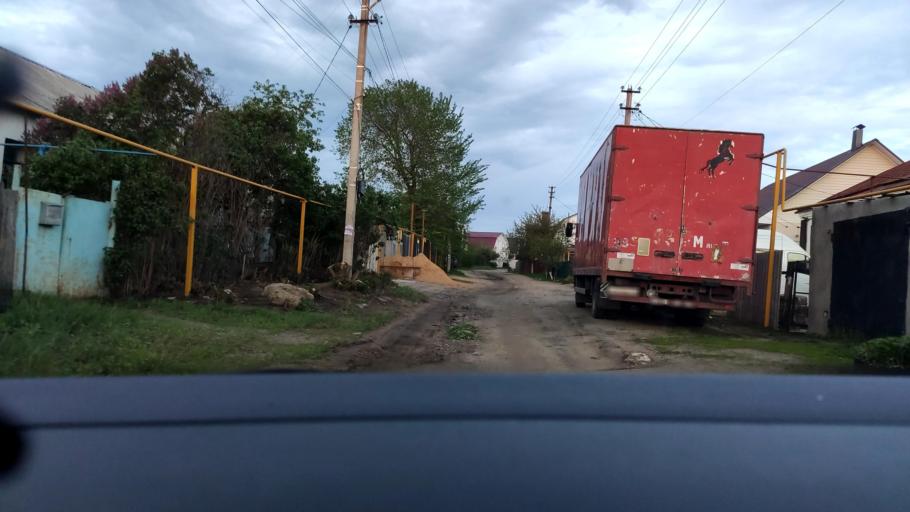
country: RU
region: Voronezj
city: Podgornoye
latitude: 51.7350
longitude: 39.1643
